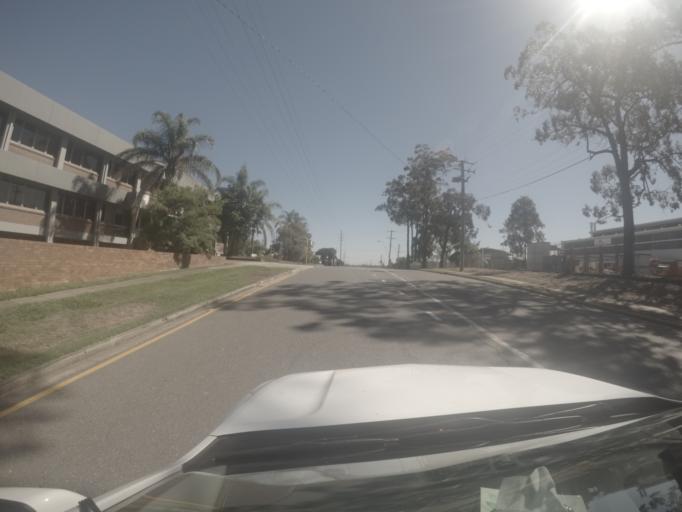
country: AU
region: Queensland
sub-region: Brisbane
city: Richlands
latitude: -27.5779
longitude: 152.9566
